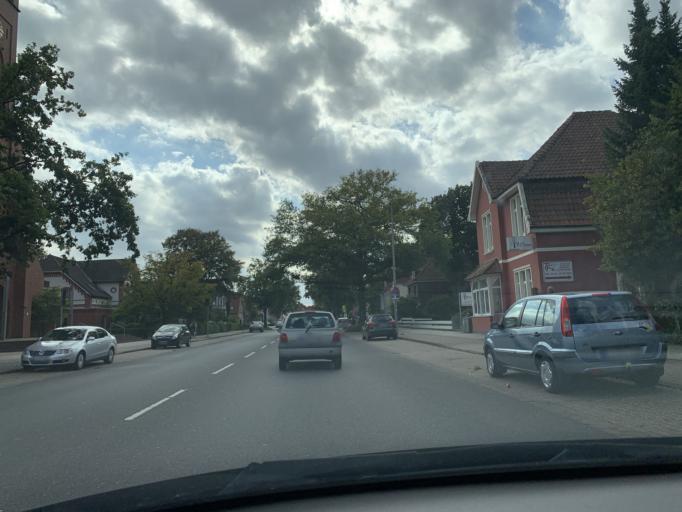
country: DE
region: Lower Saxony
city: Oldenburg
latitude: 53.1328
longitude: 8.1849
